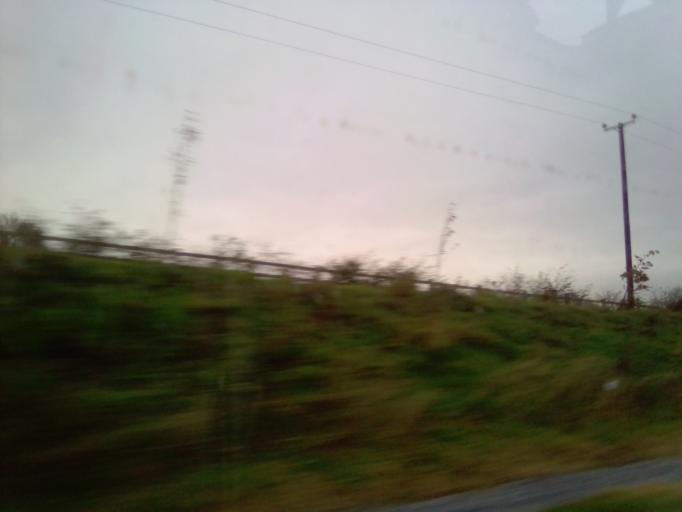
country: IE
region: Connaught
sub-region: County Galway
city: Oranmore
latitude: 53.2119
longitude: -8.8296
